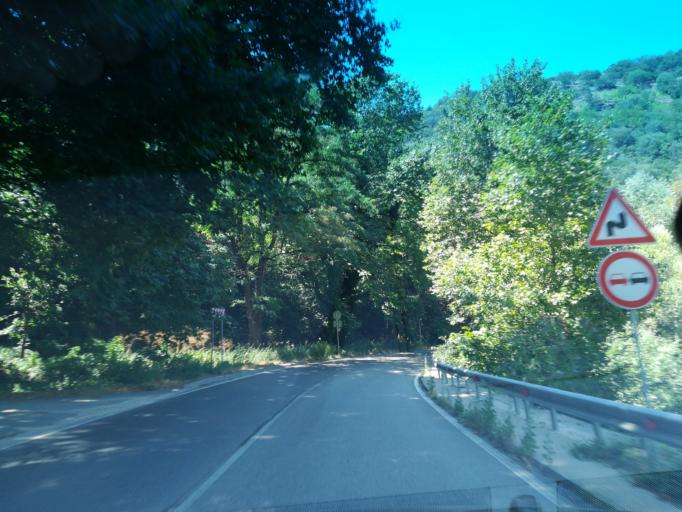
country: BG
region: Plovdiv
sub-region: Obshtina Asenovgrad
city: Asenovgrad
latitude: 41.9949
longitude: 24.8722
